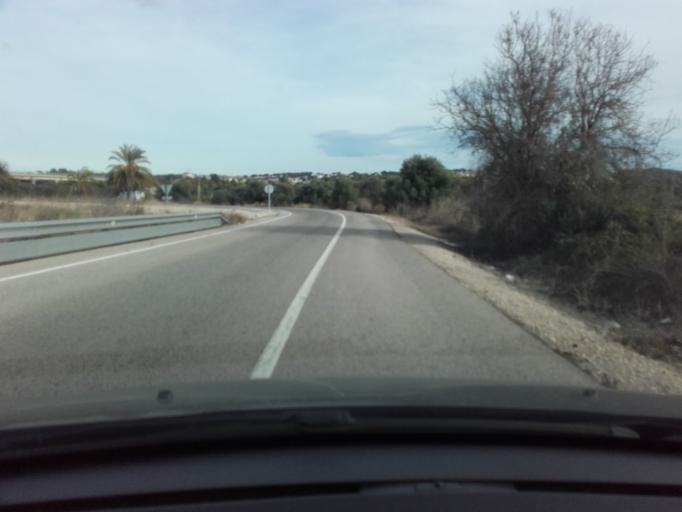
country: ES
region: Catalonia
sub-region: Provincia de Tarragona
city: El Vendrell
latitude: 41.2062
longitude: 1.5324
